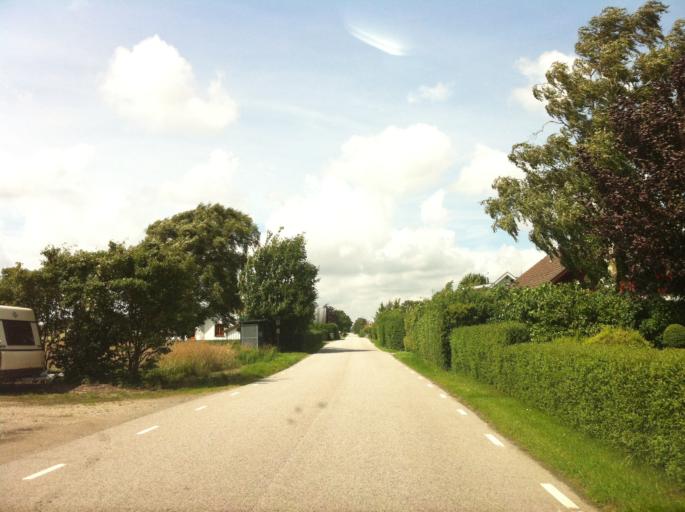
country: SE
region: Skane
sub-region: Trelleborgs Kommun
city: Anderslov
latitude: 55.4570
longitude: 13.4164
